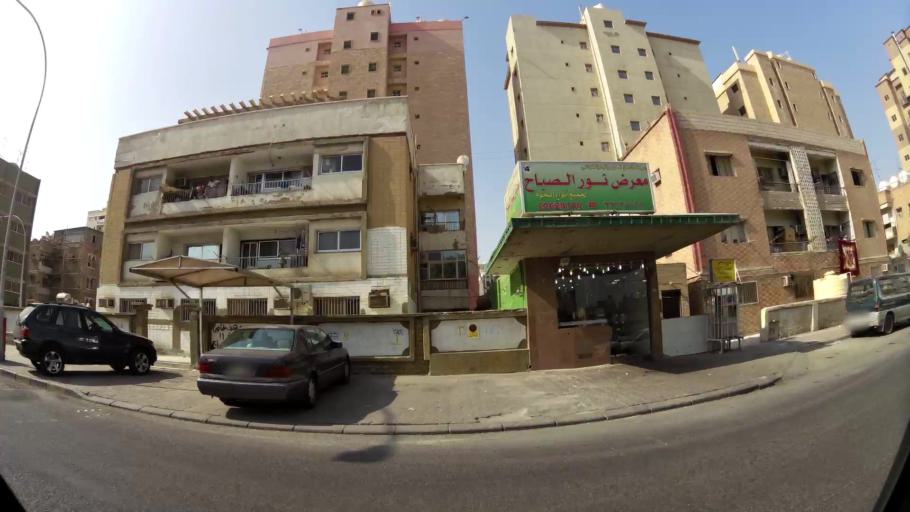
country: KW
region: Muhafazat Hawalli
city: Hawalli
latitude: 29.3388
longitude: 48.0108
